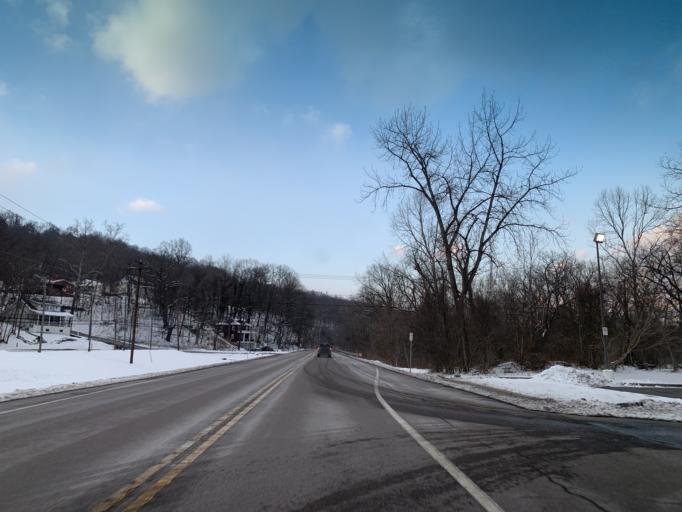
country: US
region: Maryland
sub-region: Allegany County
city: La Vale
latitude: 39.6744
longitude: -78.7918
